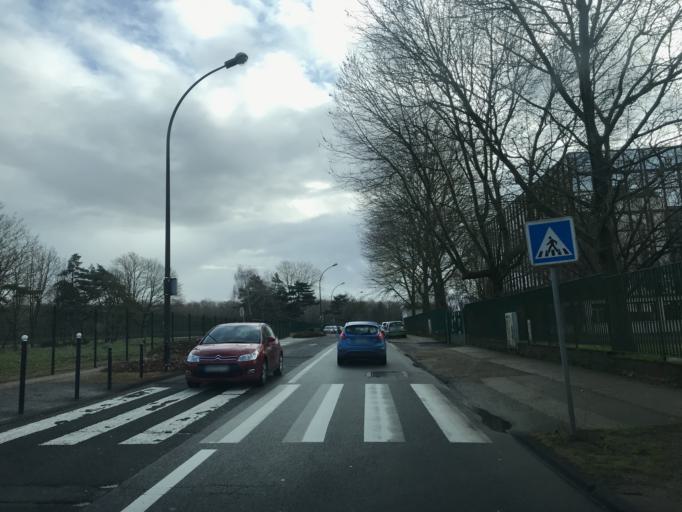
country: FR
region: Ile-de-France
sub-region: Departement des Yvelines
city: Velizy-Villacoublay
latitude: 48.7883
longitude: 2.2122
